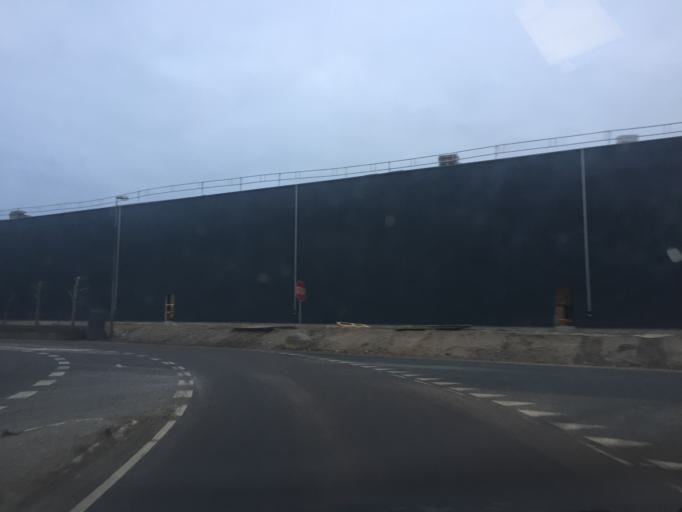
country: DK
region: Zealand
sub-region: Koge Kommune
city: Koge
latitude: 55.4643
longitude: 12.1915
